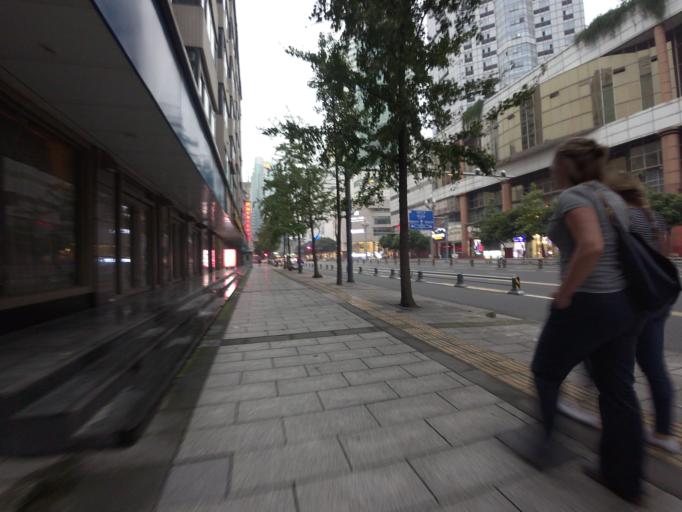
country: CN
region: Sichuan
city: Chengdu
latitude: 30.6739
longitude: 104.0648
